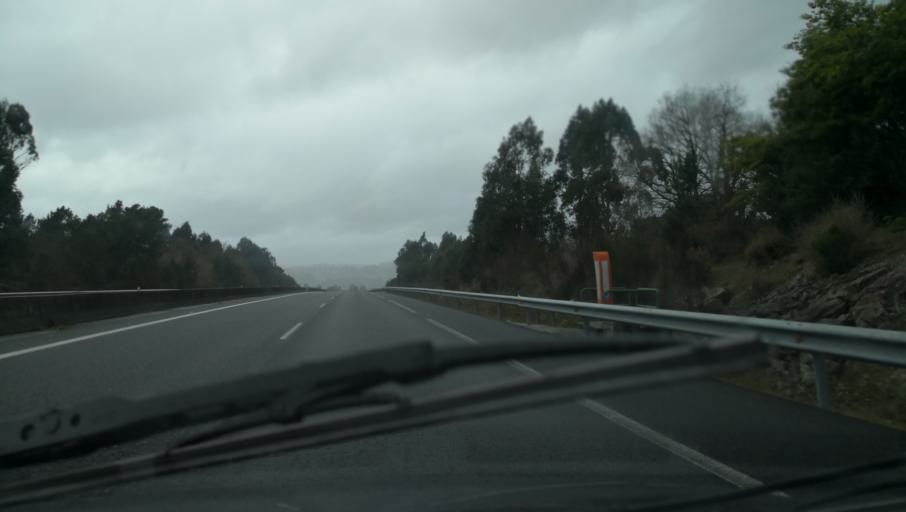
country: ES
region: Galicia
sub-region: Provincia de Pontevedra
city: Silleda
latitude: 42.6914
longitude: -8.1870
